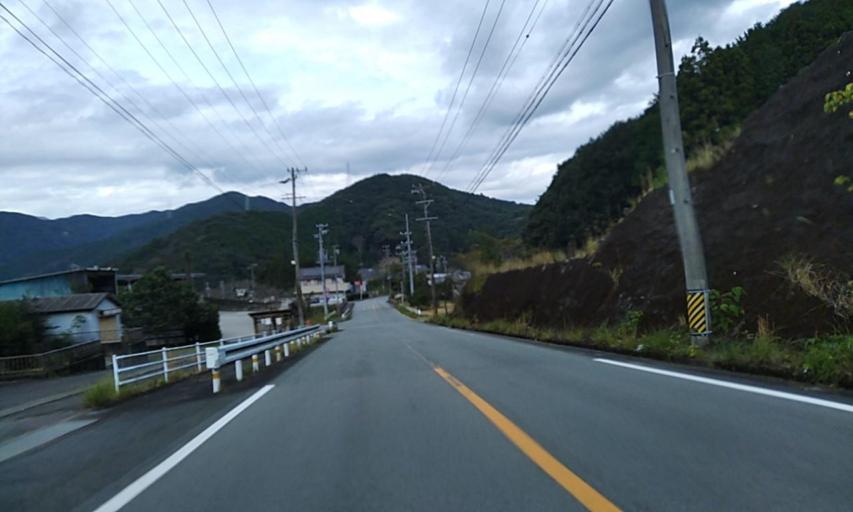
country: JP
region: Mie
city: Ise
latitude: 34.2752
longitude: 136.4921
